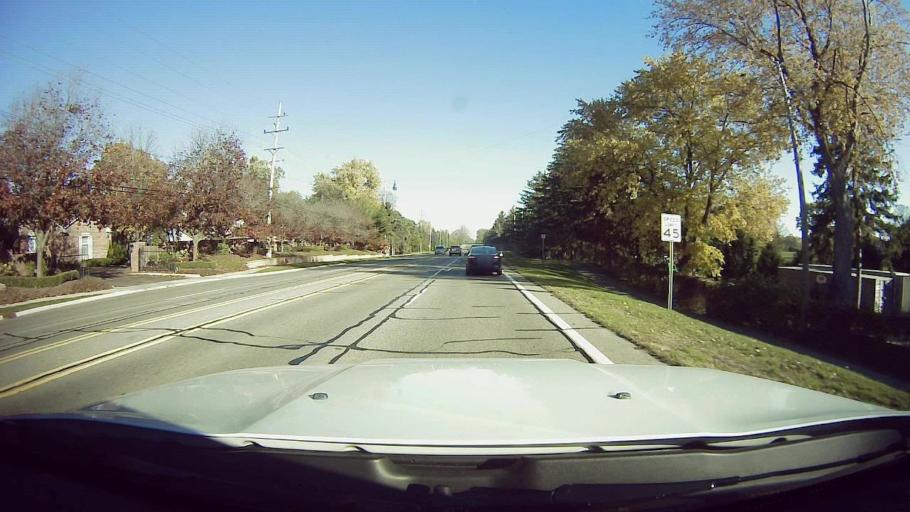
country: US
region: Michigan
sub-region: Oakland County
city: Bingham Farms
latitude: 42.5450
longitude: -83.2752
